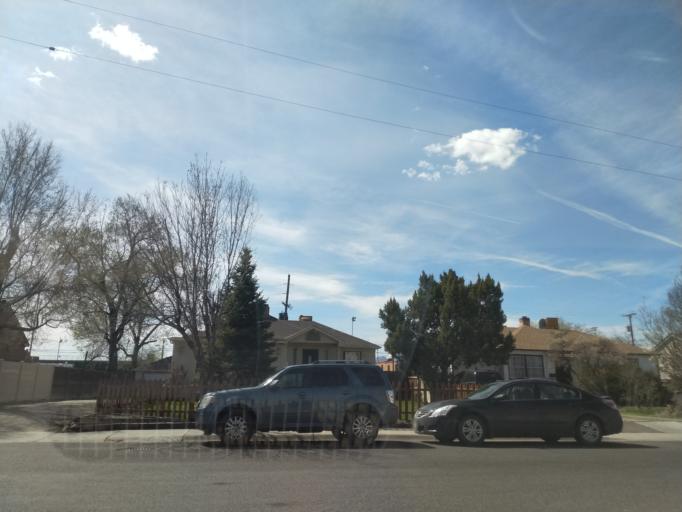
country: US
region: Colorado
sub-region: Mesa County
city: Grand Junction
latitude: 39.0784
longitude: -108.5507
